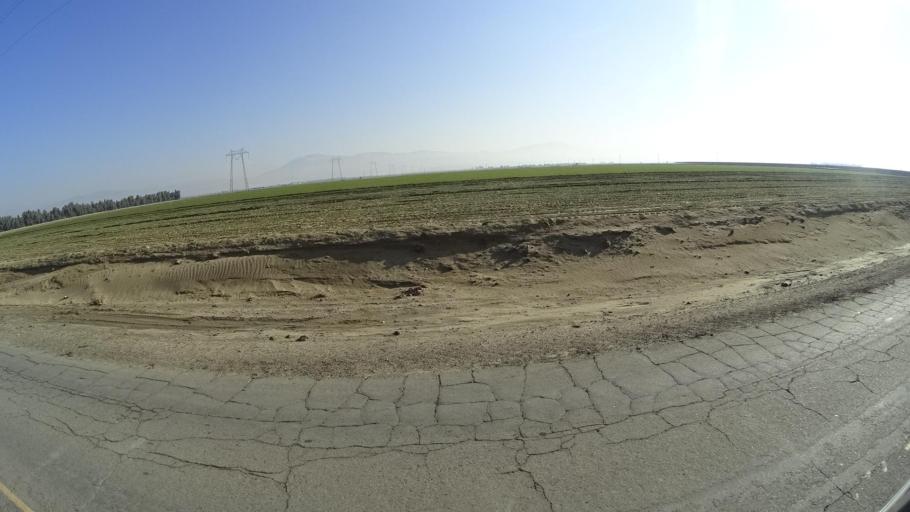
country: US
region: California
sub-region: Kern County
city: Weedpatch
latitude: 35.1237
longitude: -118.9684
